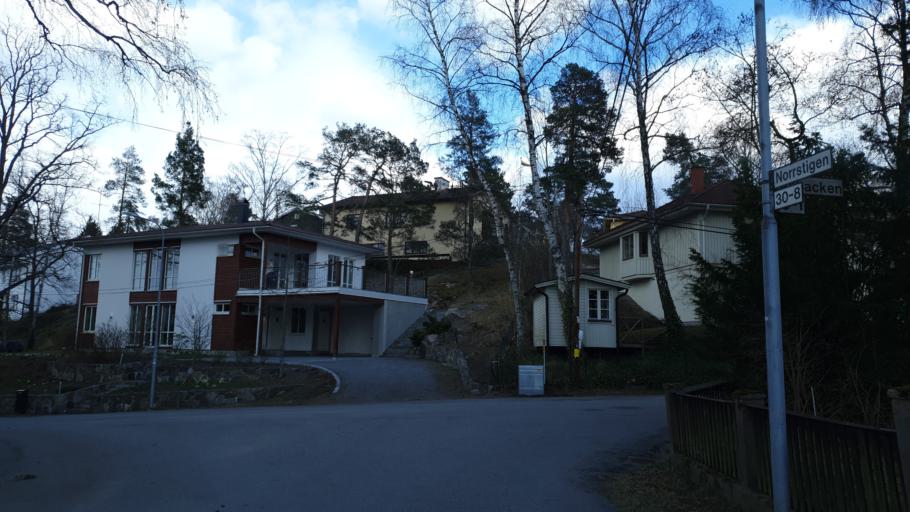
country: SE
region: Stockholm
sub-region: Lidingo
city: Lidingoe
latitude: 59.3726
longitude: 18.1205
